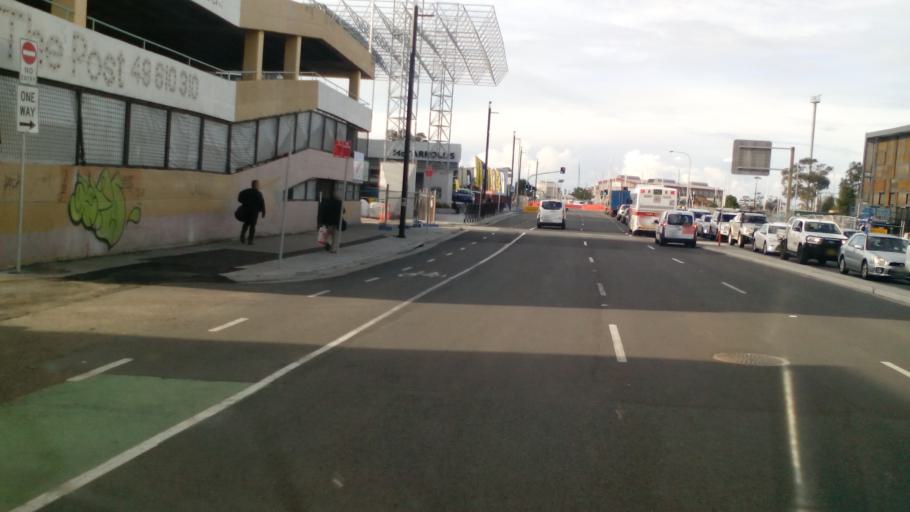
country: AU
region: New South Wales
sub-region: Newcastle
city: Carrington
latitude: -32.9246
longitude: 151.7597
